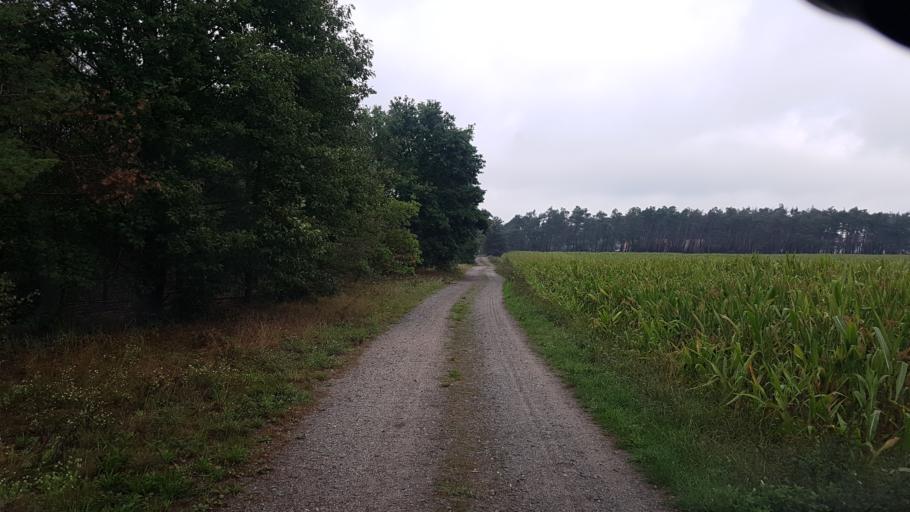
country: DE
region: Brandenburg
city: Ruckersdorf
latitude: 51.5642
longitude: 13.5628
